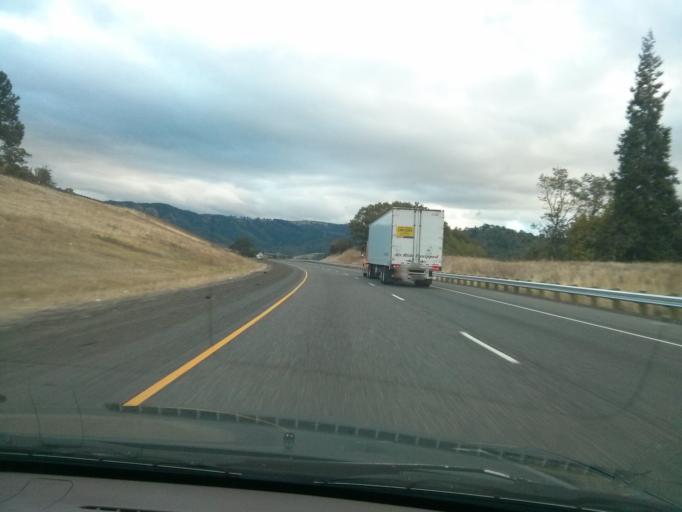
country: US
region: Oregon
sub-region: Douglas County
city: Winston
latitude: 43.0909
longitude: -123.3685
